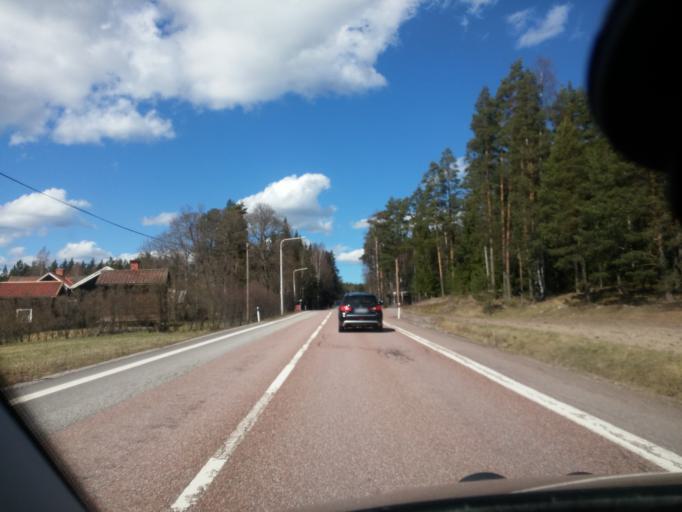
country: SE
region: Dalarna
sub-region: Faluns Kommun
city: Svardsjo
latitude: 60.7267
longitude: 15.7682
